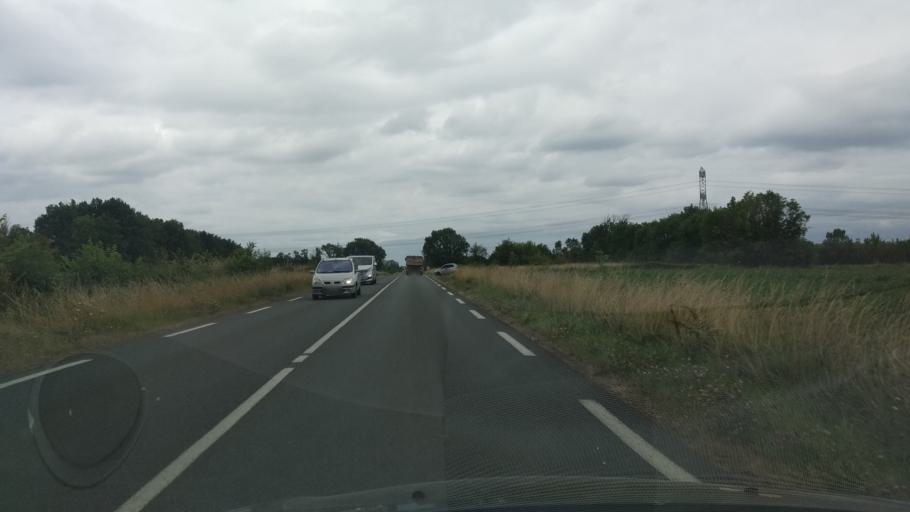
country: FR
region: Poitou-Charentes
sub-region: Departement de la Vienne
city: Saint-Maurice-la-Clouere
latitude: 46.3928
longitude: 0.3994
